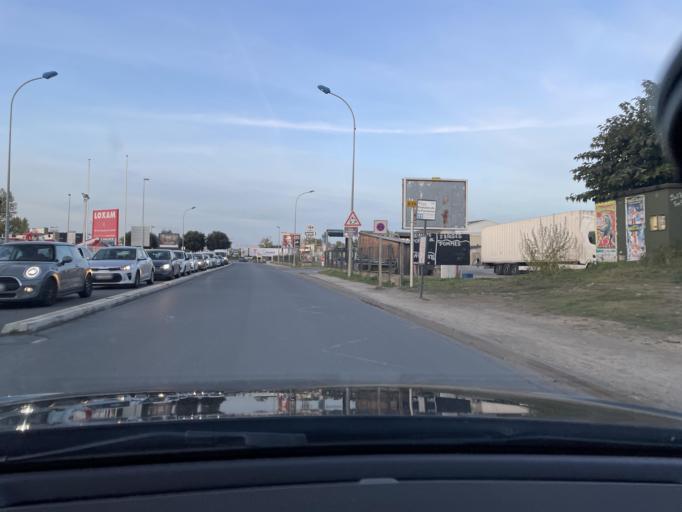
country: FR
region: Aquitaine
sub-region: Departement de la Gironde
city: Villenave-d'Ornon
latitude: 44.7895
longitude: -0.5354
